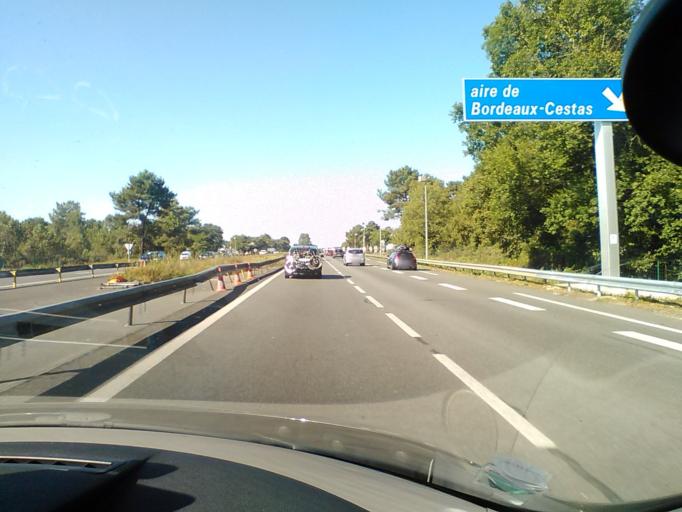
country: FR
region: Aquitaine
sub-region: Departement de la Gironde
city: Saint-Aubin-de-Medoc
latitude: 44.7478
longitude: -0.6991
